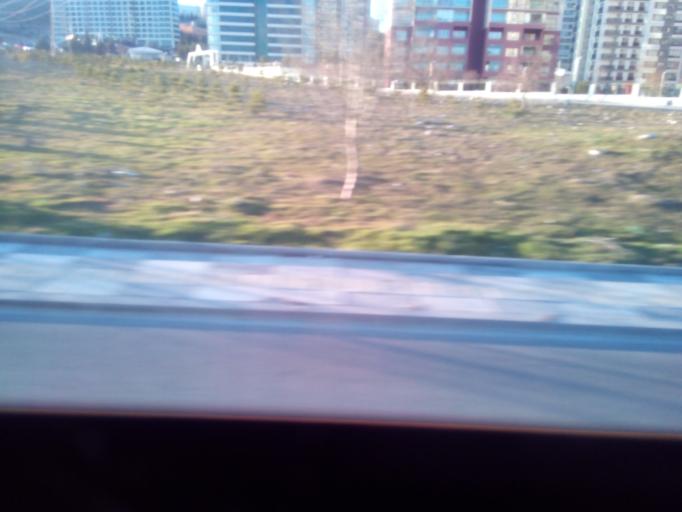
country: TR
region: Ankara
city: Etimesgut
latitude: 39.8824
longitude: 32.6597
